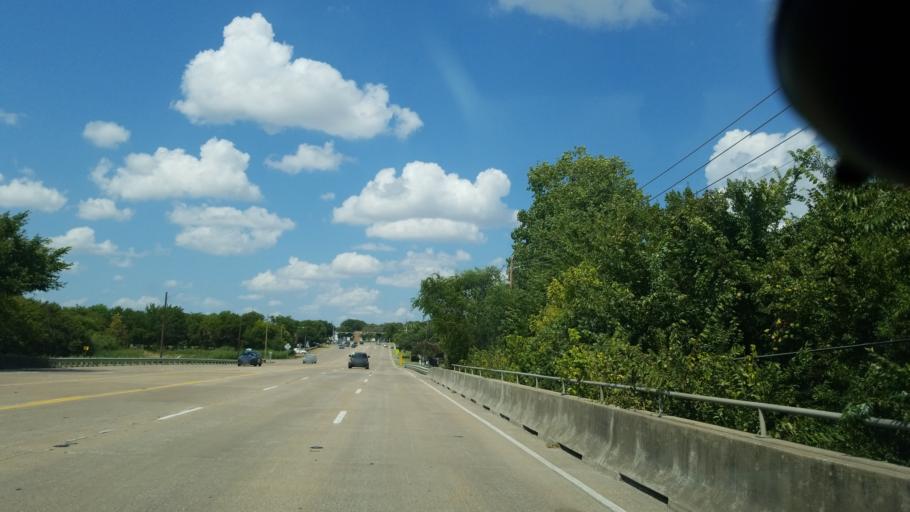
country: US
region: Texas
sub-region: Dallas County
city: Grand Prairie
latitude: 32.7318
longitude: -96.9941
